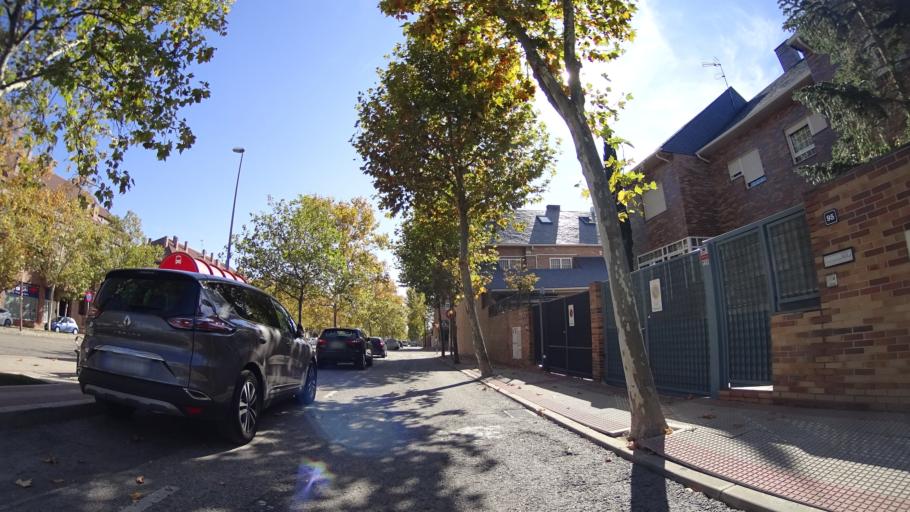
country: ES
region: Madrid
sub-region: Provincia de Madrid
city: Villanueva del Pardillo
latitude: 40.5017
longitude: -3.9688
